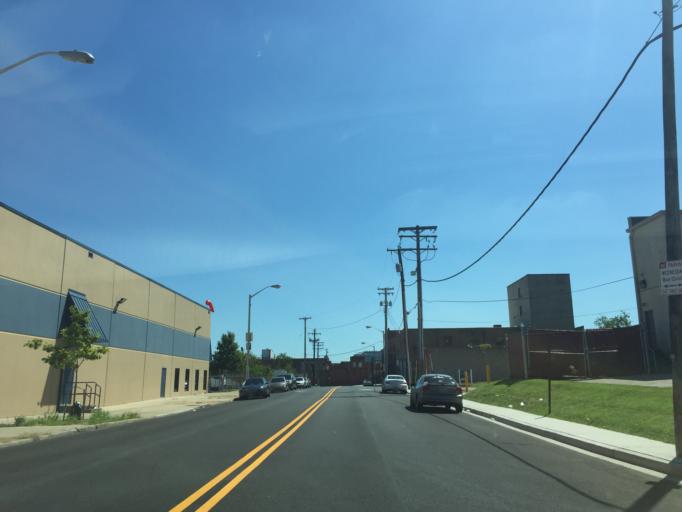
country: US
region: Maryland
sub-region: City of Baltimore
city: Baltimore
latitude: 39.2927
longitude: -76.5649
